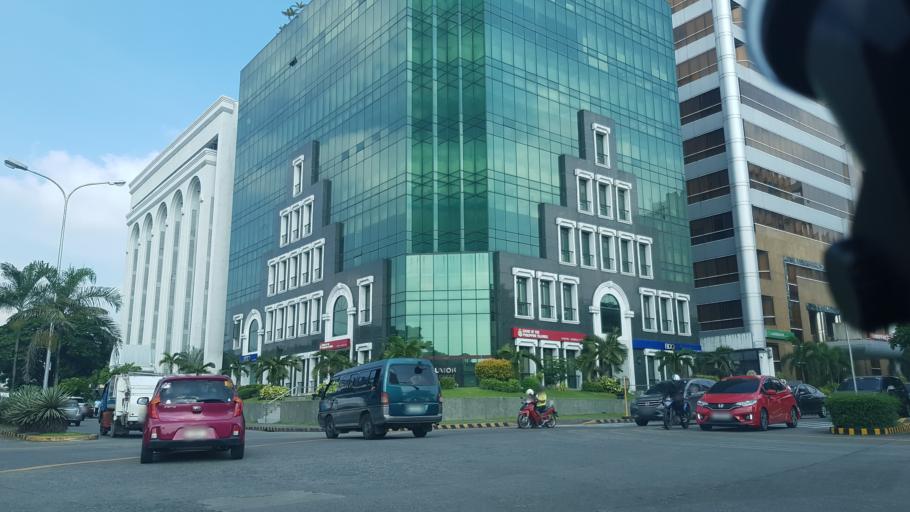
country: PH
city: Sambayanihan People's Village
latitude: 14.4235
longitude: 121.0241
